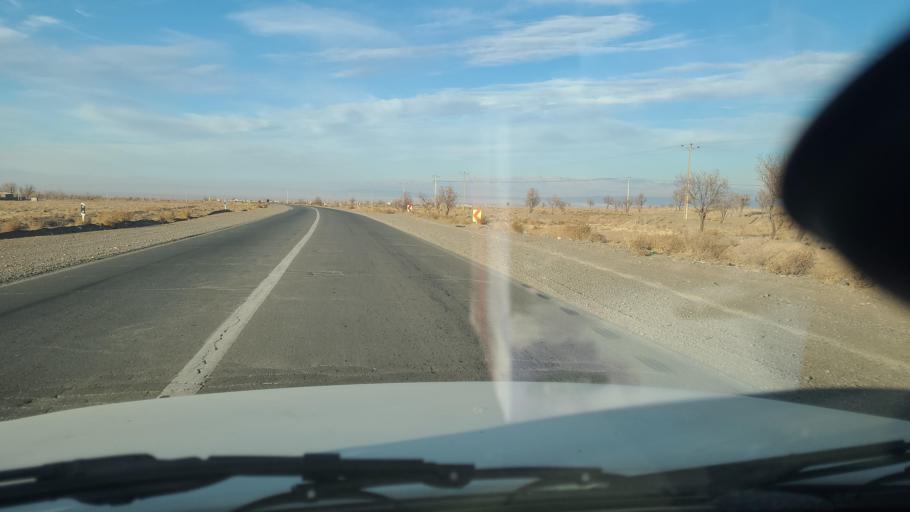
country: IR
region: Razavi Khorasan
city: Neqab
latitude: 36.4924
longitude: 57.5317
